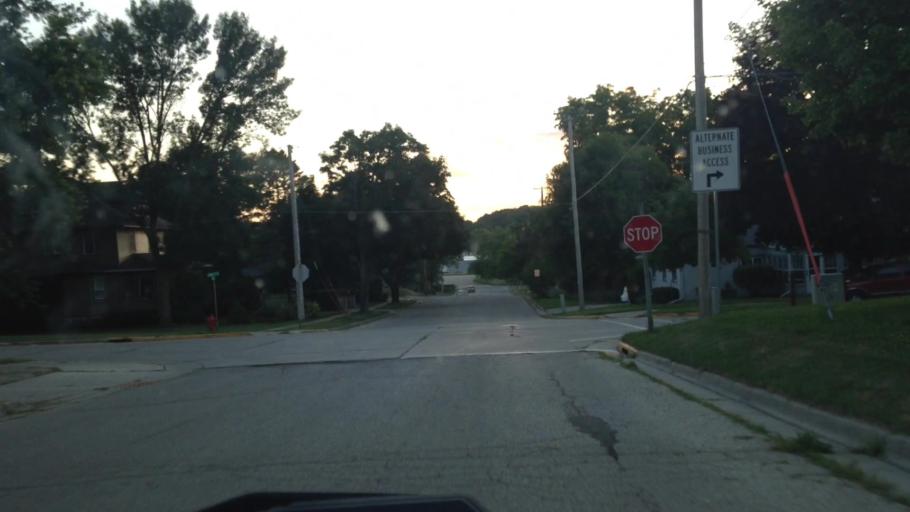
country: US
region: Wisconsin
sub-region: Dodge County
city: Mayville
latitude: 43.4904
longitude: -88.5466
